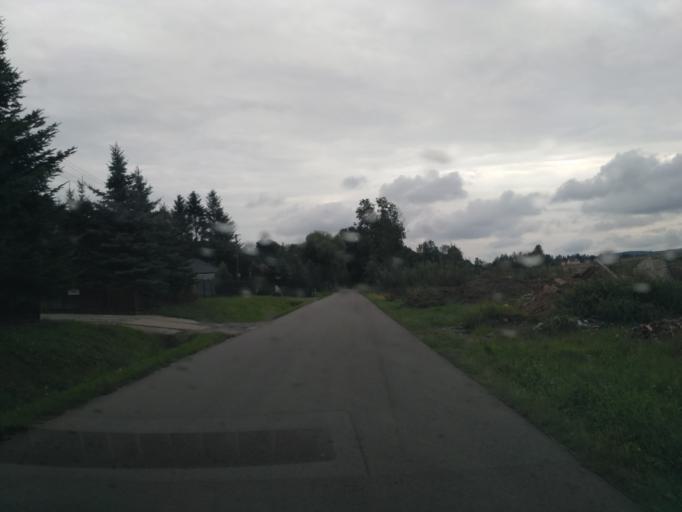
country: PL
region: Subcarpathian Voivodeship
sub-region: Powiat ropczycko-sedziszowski
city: Iwierzyce
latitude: 50.0258
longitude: 21.7750
